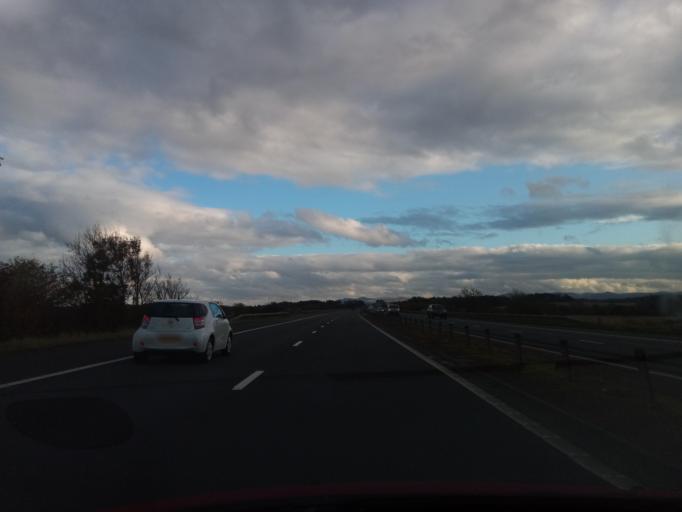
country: GB
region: Scotland
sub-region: West Lothian
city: Broxburn
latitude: 55.9710
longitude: -3.4590
